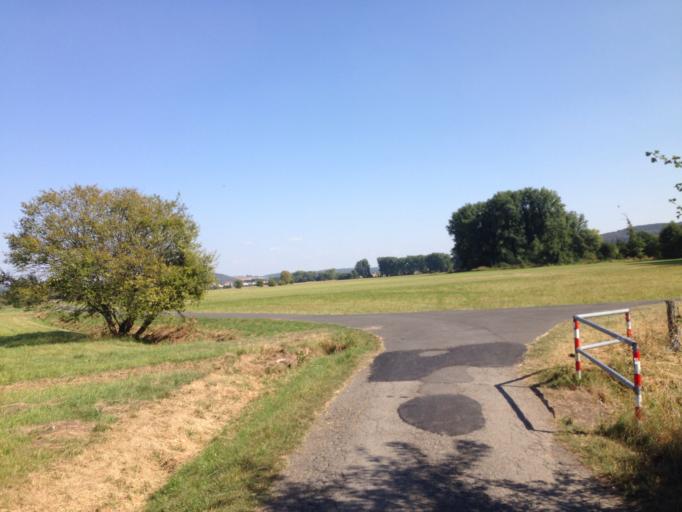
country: DE
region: Hesse
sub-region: Regierungsbezirk Giessen
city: Alten Buseck
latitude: 50.6070
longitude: 8.7232
